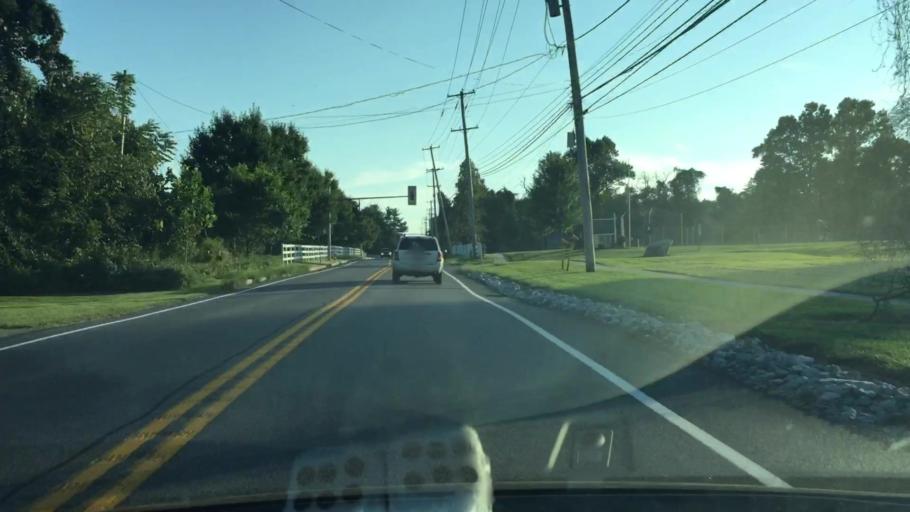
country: US
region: Pennsylvania
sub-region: Delaware County
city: Chester Heights
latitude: 39.8479
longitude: -75.4867
